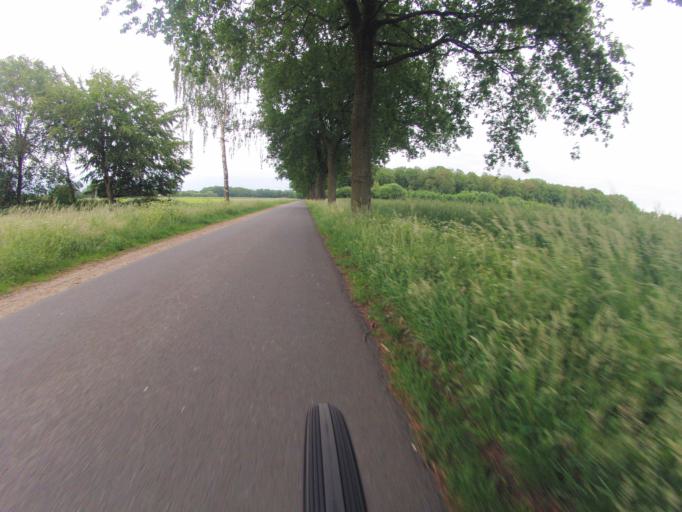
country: DE
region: North Rhine-Westphalia
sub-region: Regierungsbezirk Munster
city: Saerbeck
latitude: 52.1733
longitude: 7.6066
